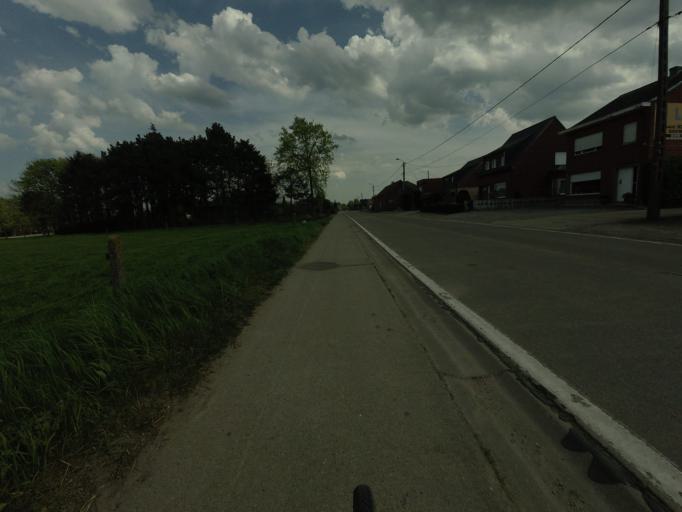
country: BE
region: Flanders
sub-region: Provincie Antwerpen
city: Putte
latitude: 51.0682
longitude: 4.6204
